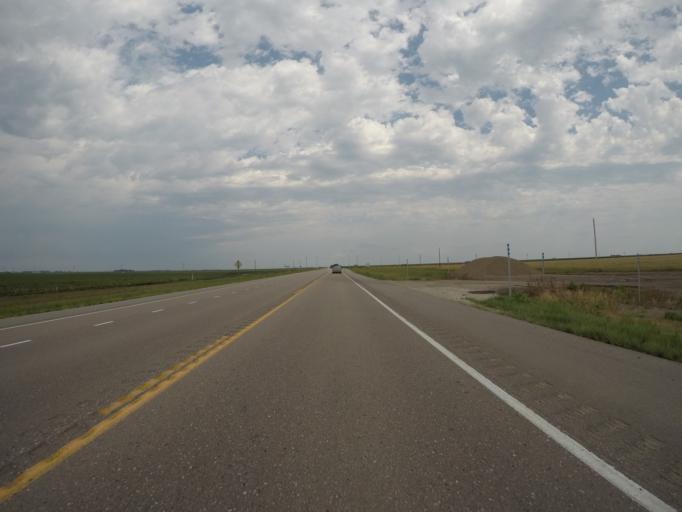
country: US
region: Nebraska
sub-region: Clay County
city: Harvard
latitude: 40.5827
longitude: -98.1127
